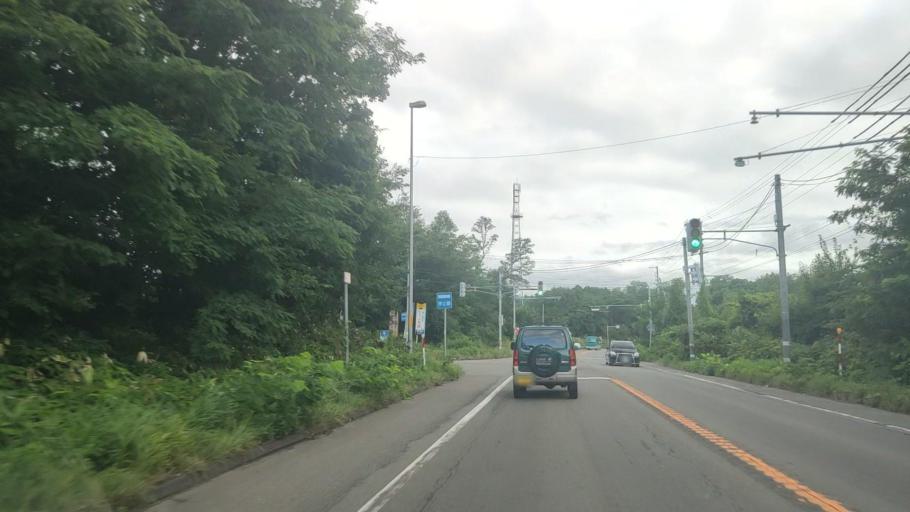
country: JP
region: Hokkaido
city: Nanae
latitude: 42.0677
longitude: 140.6032
